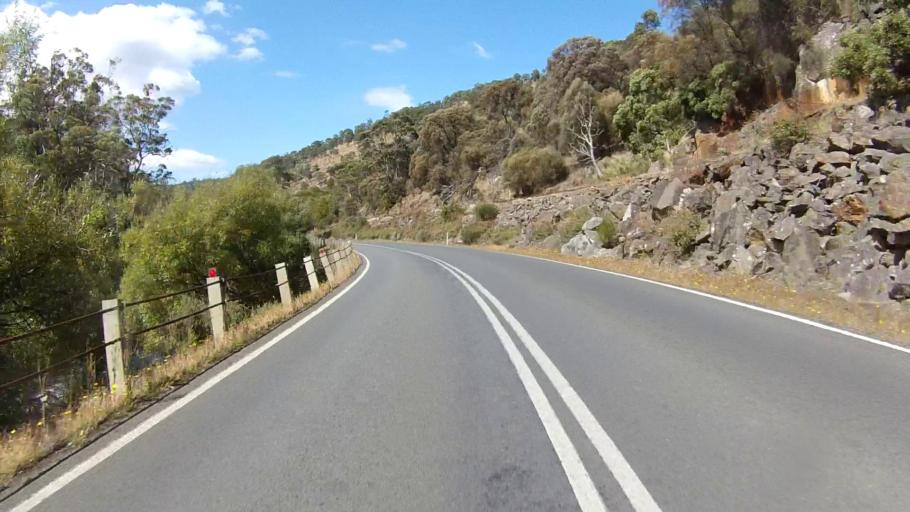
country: AU
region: Tasmania
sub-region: Derwent Valley
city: New Norfolk
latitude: -42.6814
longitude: 146.7664
